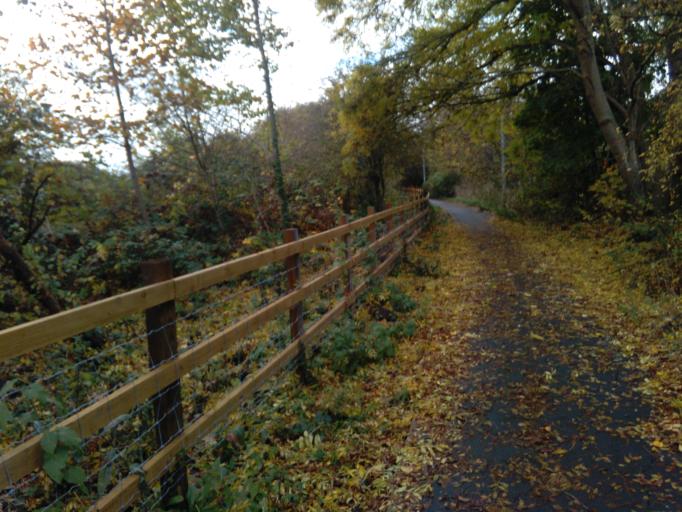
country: GB
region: England
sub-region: Greater London
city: Feltham
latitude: 51.4466
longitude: -0.4260
